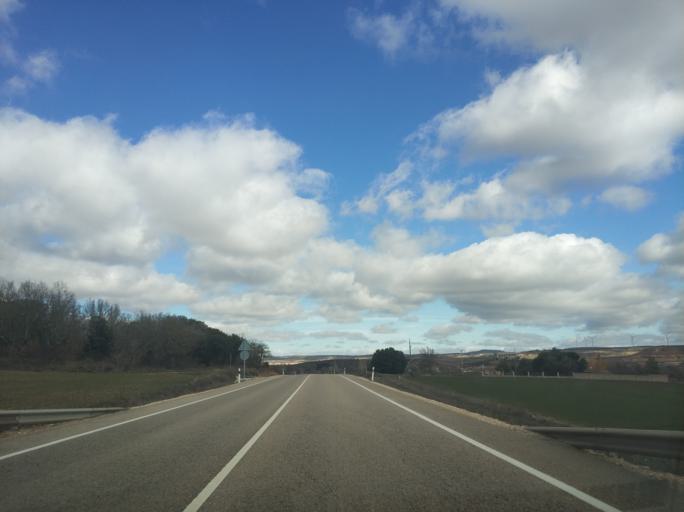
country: ES
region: Castille and Leon
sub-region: Provincia de Burgos
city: Revillarruz
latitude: 42.2207
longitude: -3.6534
